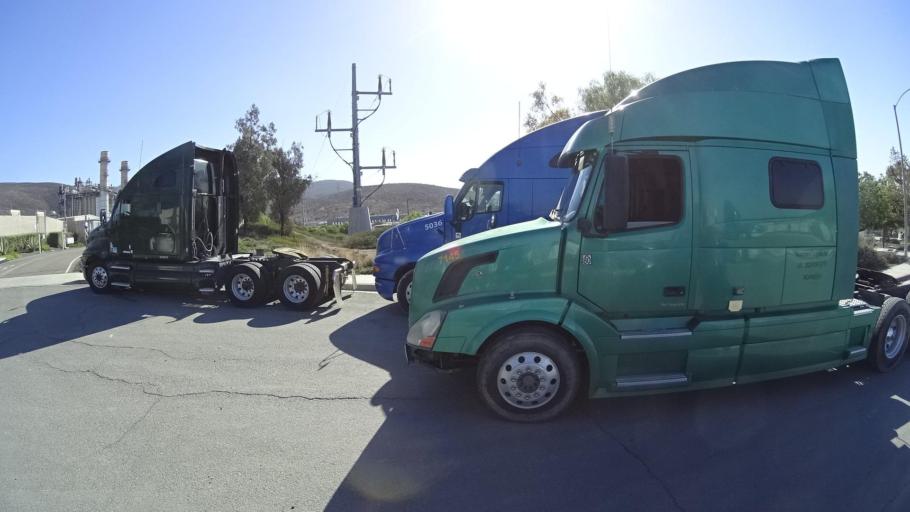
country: MX
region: Baja California
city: Tijuana
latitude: 32.5721
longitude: -116.9167
